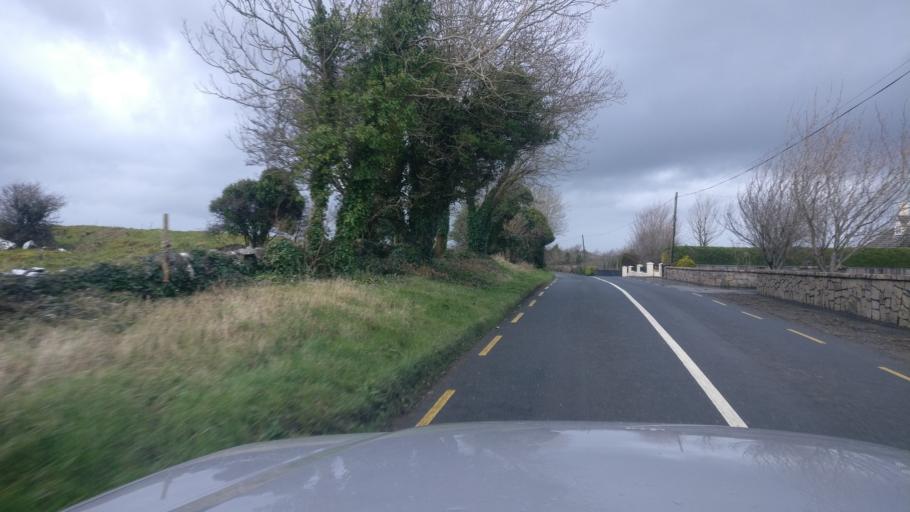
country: IE
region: Connaught
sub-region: County Galway
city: Loughrea
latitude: 53.1713
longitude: -8.6828
